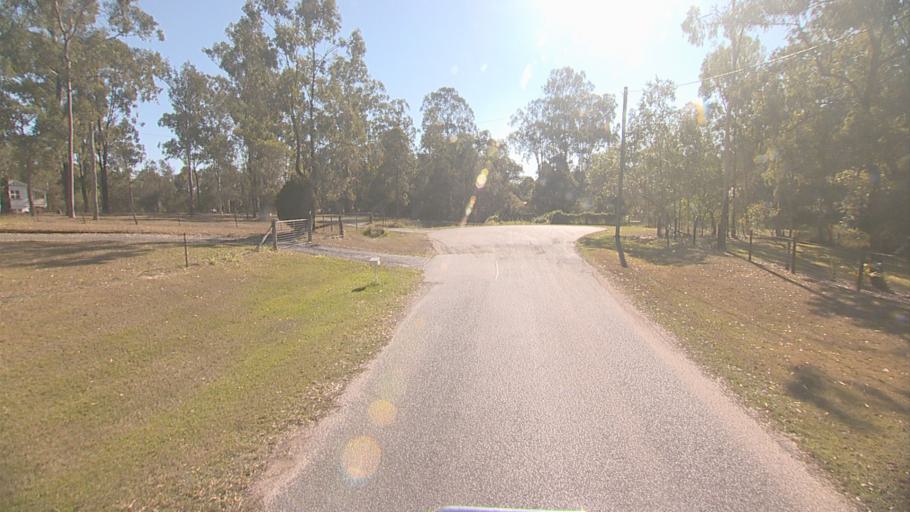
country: AU
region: Queensland
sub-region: Logan
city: North Maclean
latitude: -27.8249
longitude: 153.0483
